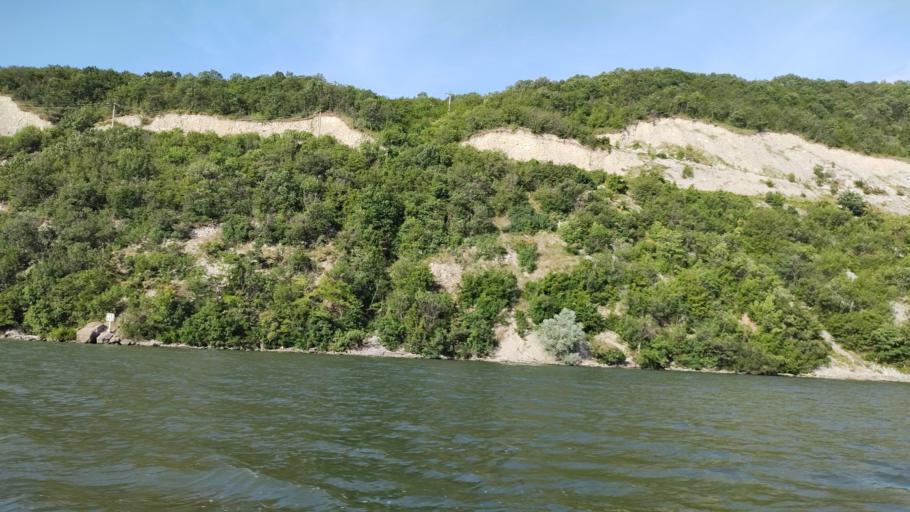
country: RO
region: Mehedinti
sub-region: Comuna Svinita
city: Svinita
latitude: 44.5061
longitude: 22.0820
